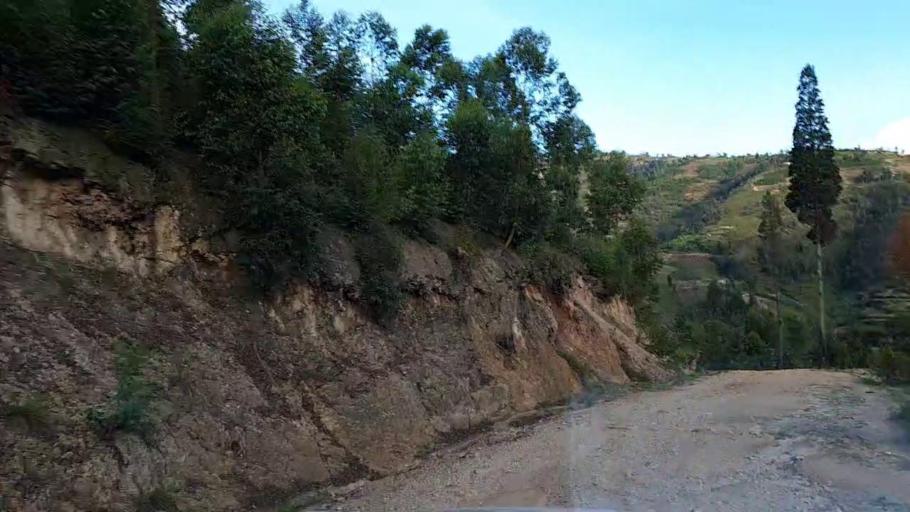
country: RW
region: Southern Province
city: Gikongoro
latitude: -2.4007
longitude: 29.5635
